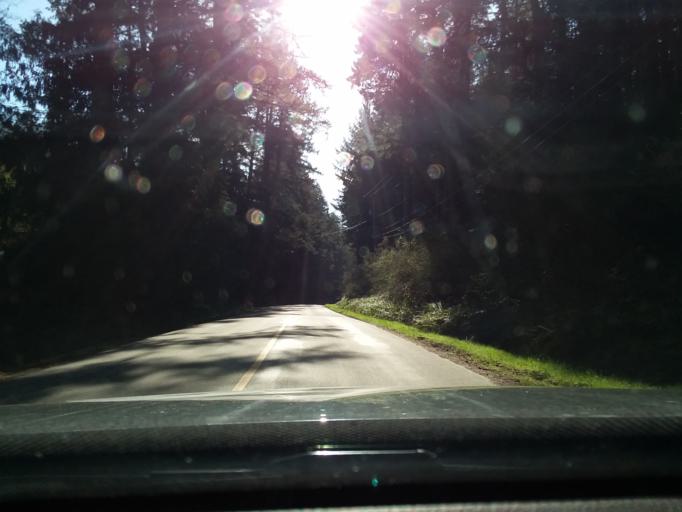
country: CA
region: British Columbia
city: North Cowichan
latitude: 48.9389
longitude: -123.4916
